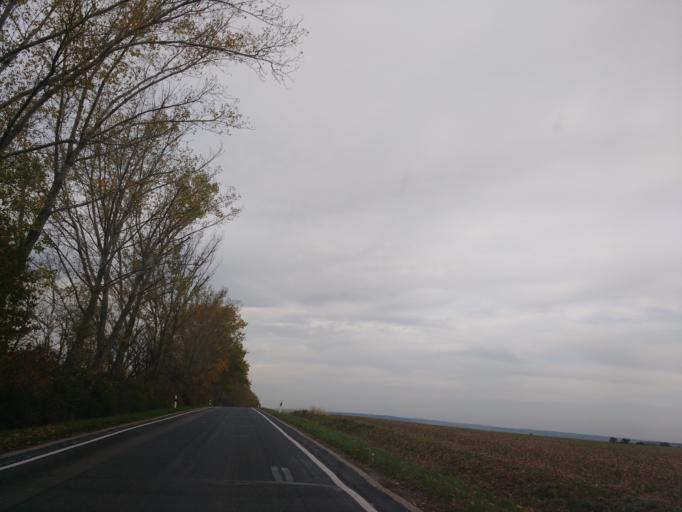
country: DE
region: Thuringia
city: Seebach
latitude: 51.1510
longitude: 10.5200
